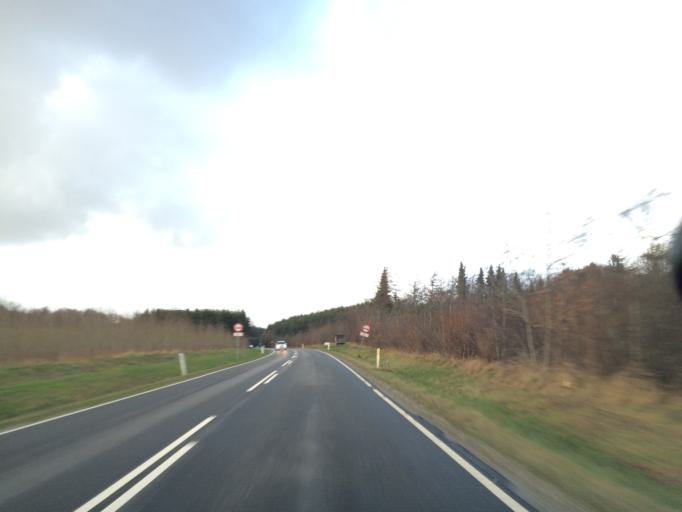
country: DK
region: Central Jutland
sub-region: Silkeborg Kommune
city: Svejbaek
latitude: 56.0945
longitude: 9.6550
